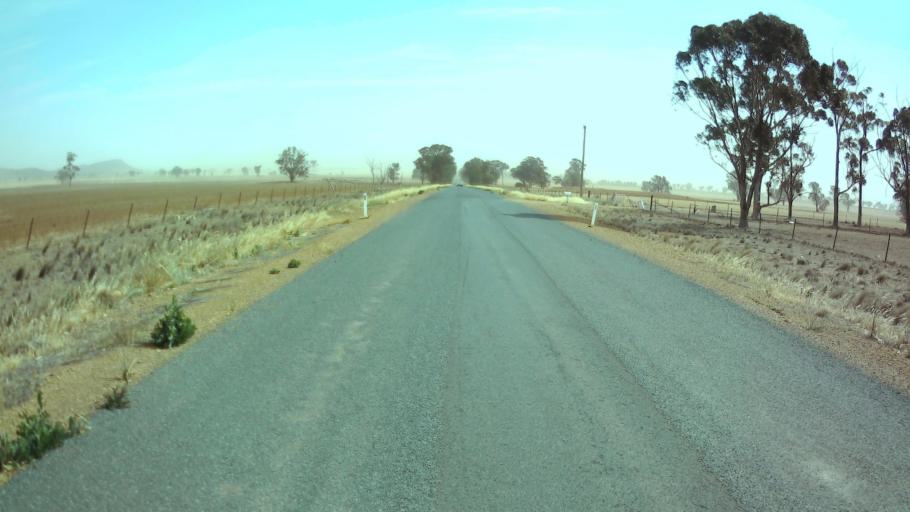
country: AU
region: New South Wales
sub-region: Weddin
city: Grenfell
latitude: -33.7654
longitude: 147.9879
